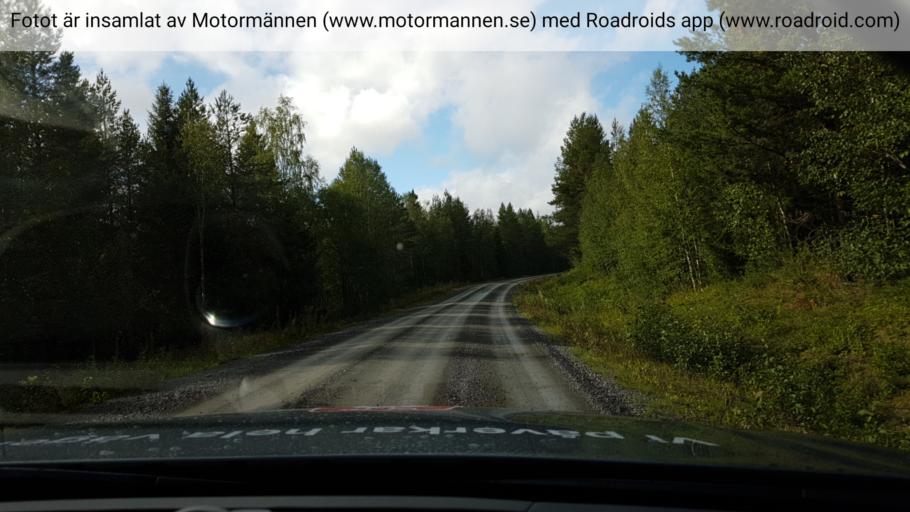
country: SE
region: Jaemtland
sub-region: Krokoms Kommun
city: Krokom
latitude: 63.7036
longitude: 14.5384
